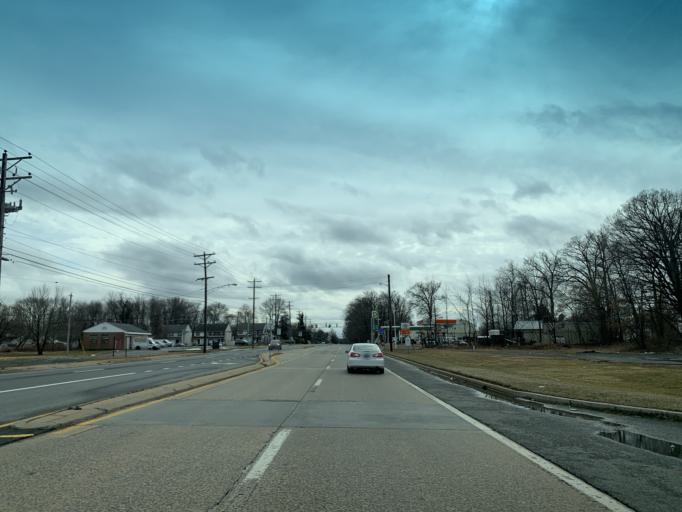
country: US
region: Delaware
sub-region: New Castle County
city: New Castle
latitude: 39.6852
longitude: -75.5576
